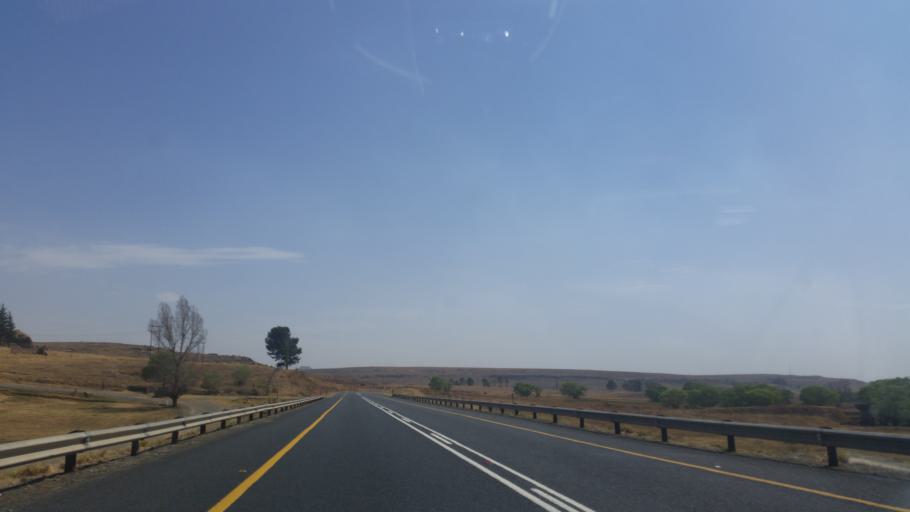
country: ZA
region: Orange Free State
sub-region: Thabo Mofutsanyana District Municipality
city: Bethlehem
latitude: -28.3084
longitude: 28.4981
